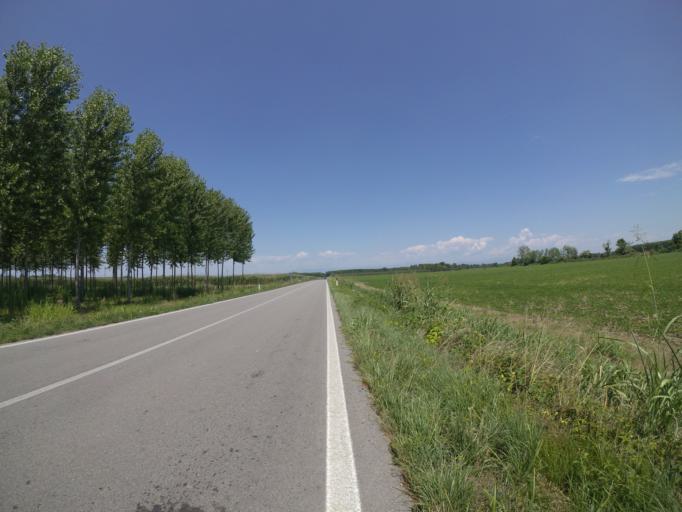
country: IT
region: Friuli Venezia Giulia
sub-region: Provincia di Udine
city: Talmassons
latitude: 45.9018
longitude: 13.1349
